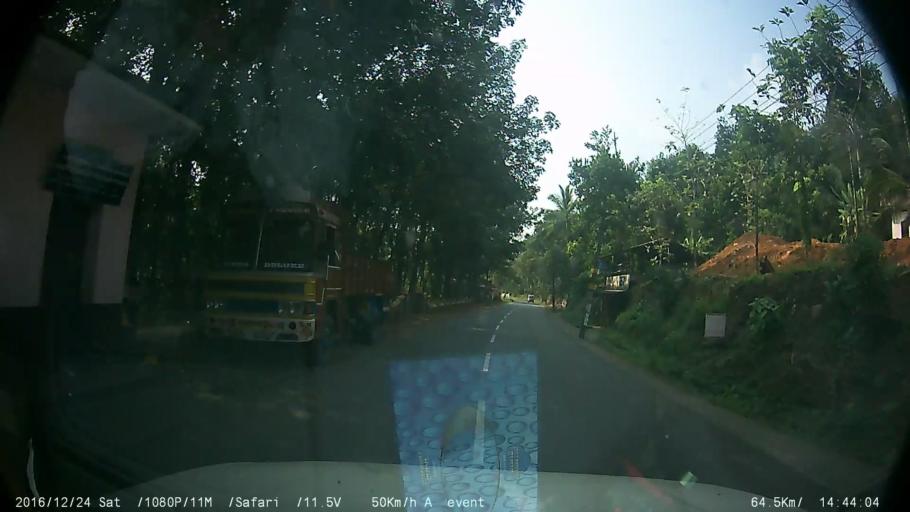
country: IN
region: Kerala
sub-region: Kottayam
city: Lalam
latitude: 9.7766
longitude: 76.7231
